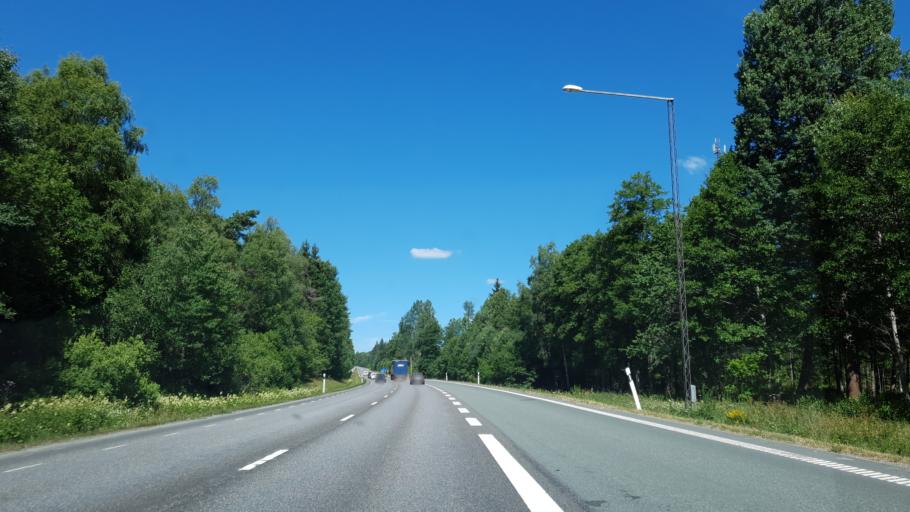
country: SE
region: Joenkoeping
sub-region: Varnamo Kommun
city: Rydaholm
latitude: 56.9874
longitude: 14.2993
